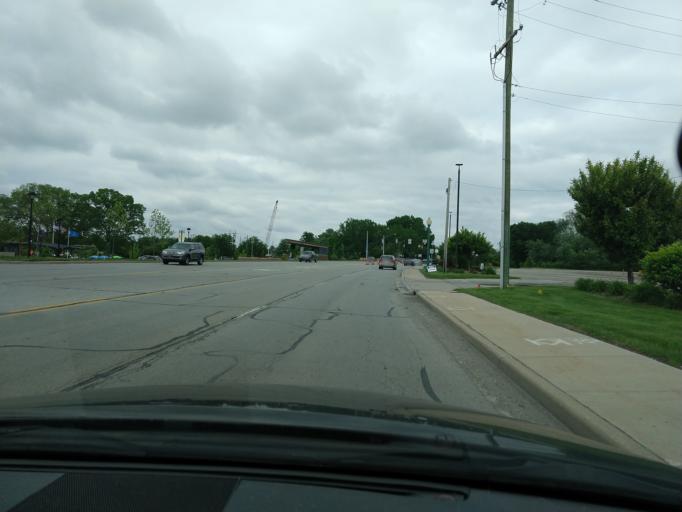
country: US
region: Indiana
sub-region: Hamilton County
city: Noblesville
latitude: 40.0469
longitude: -86.0210
